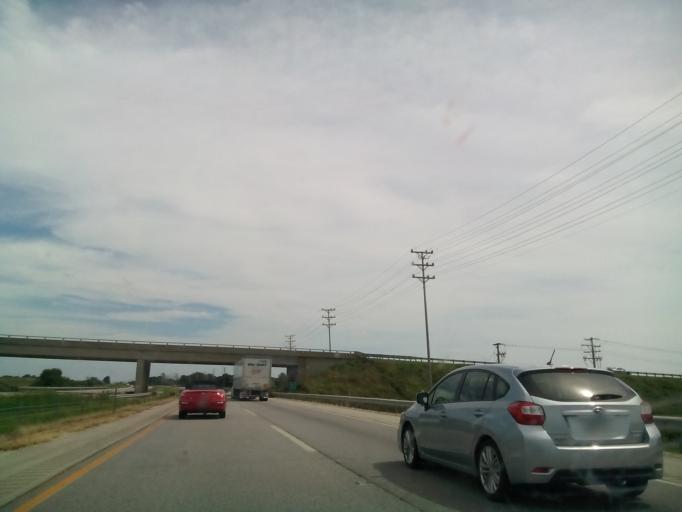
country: US
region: Illinois
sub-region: Kane County
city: Sugar Grove
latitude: 41.8030
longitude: -88.4293
